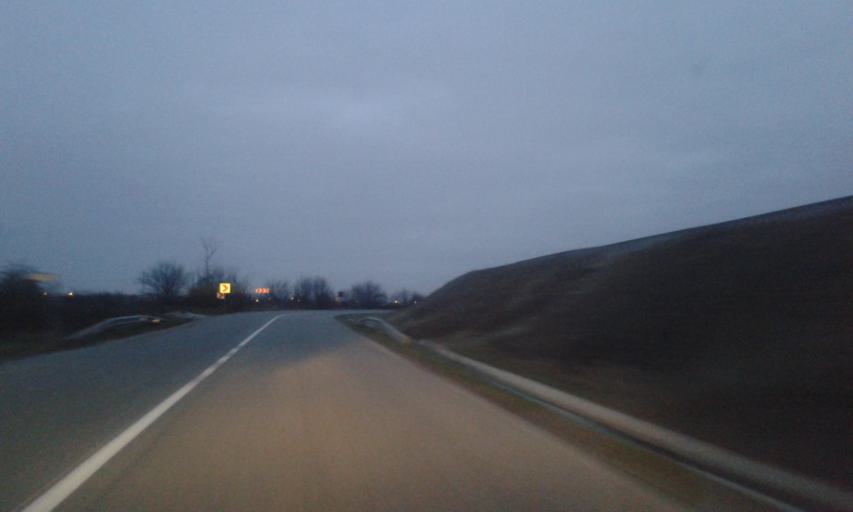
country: RO
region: Gorj
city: Targu Jiu
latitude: 45.0700
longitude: 23.2842
